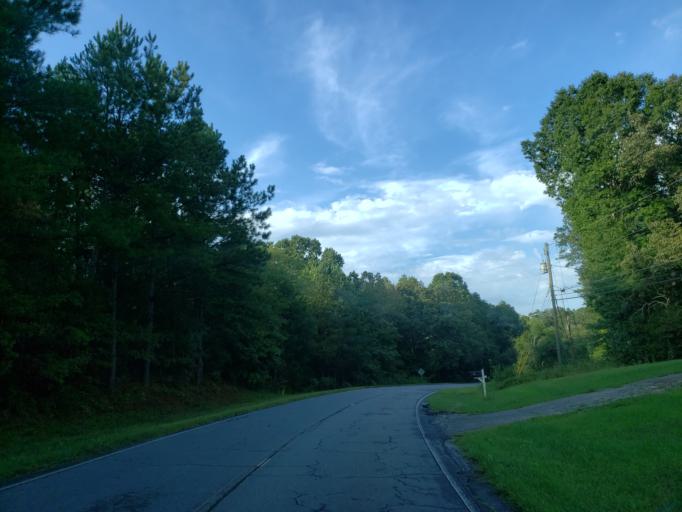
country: US
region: Georgia
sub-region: Bartow County
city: Euharlee
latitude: 34.2267
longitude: -84.9681
